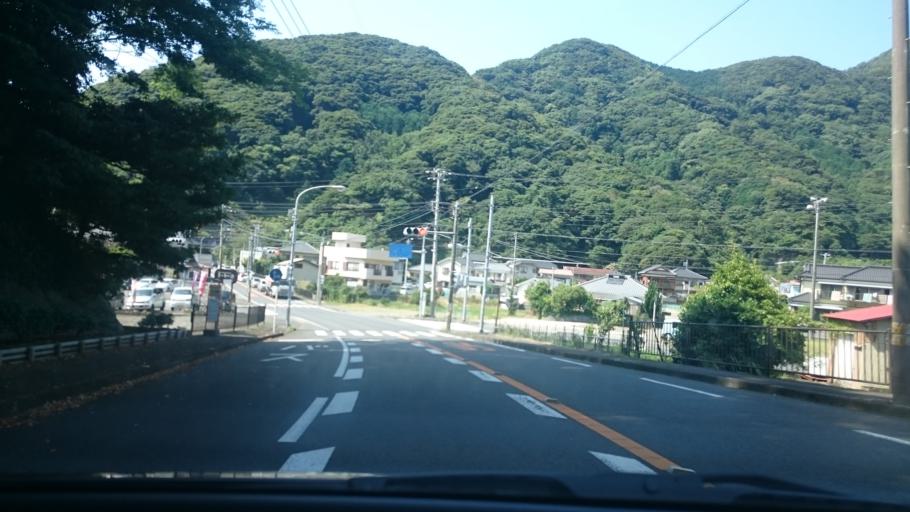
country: JP
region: Shizuoka
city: Heda
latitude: 34.8256
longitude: 138.7722
